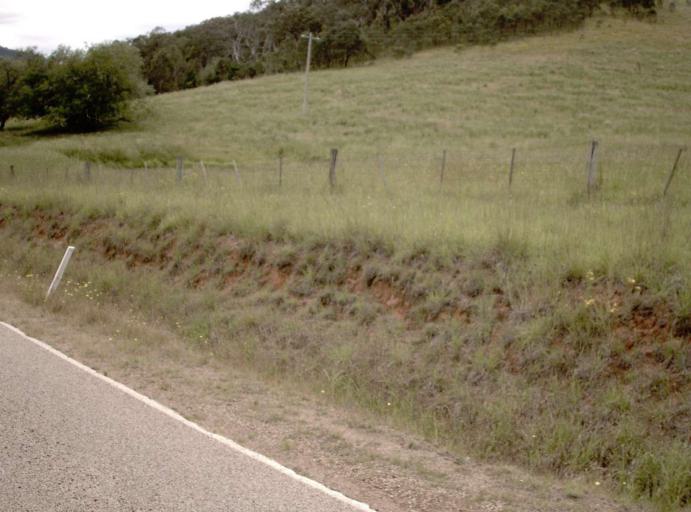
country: AU
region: Victoria
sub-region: East Gippsland
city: Bairnsdale
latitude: -37.5450
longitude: 147.2026
